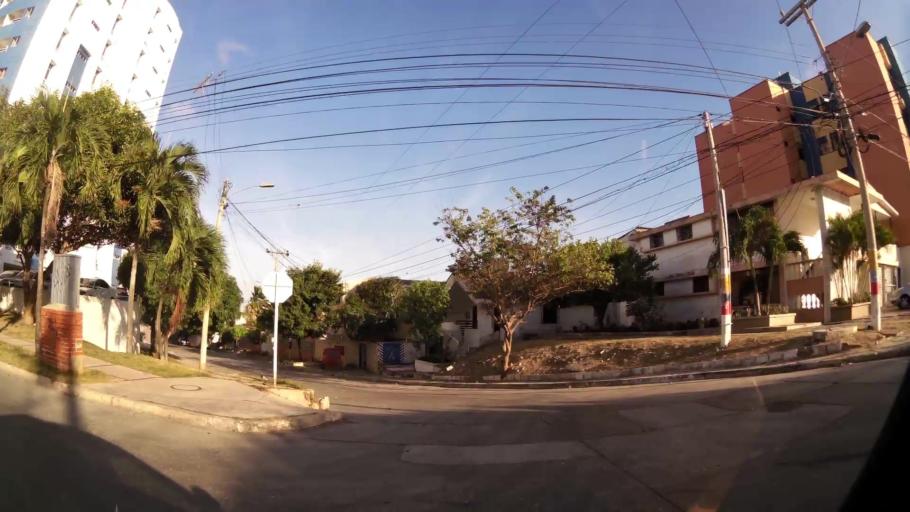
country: CO
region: Atlantico
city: Barranquilla
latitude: 10.9829
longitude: -74.8051
